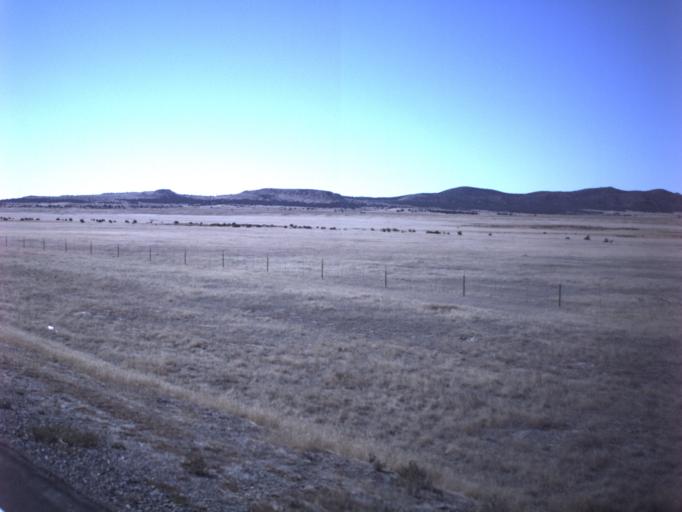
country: US
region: Utah
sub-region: Tooele County
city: Grantsville
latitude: 40.2849
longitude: -112.7420
